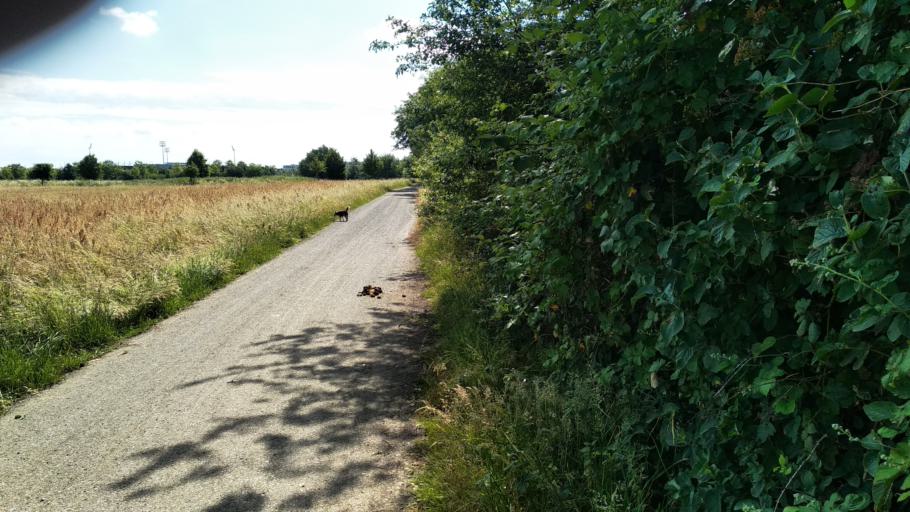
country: DE
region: North Rhine-Westphalia
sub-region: Regierungsbezirk Dusseldorf
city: Monchengladbach
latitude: 51.1777
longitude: 6.3787
